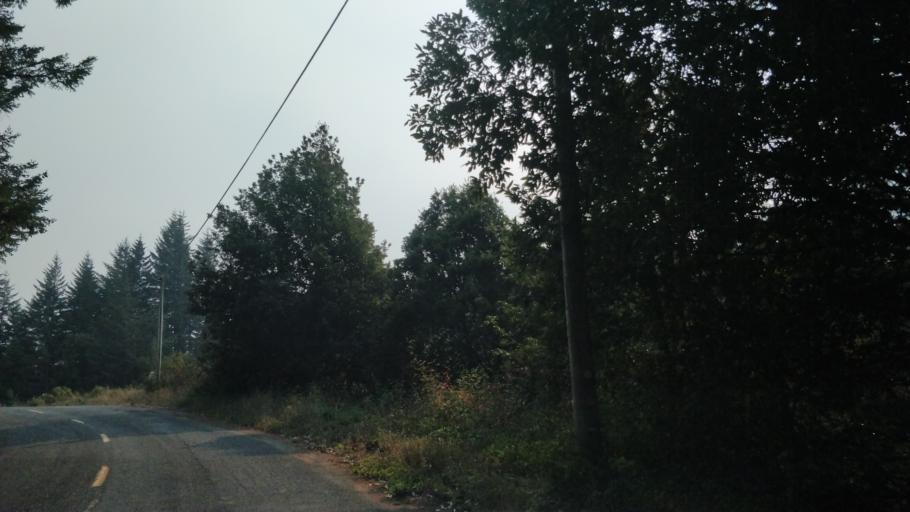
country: US
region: California
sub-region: Humboldt County
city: Rio Dell
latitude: 40.3011
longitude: -124.2504
